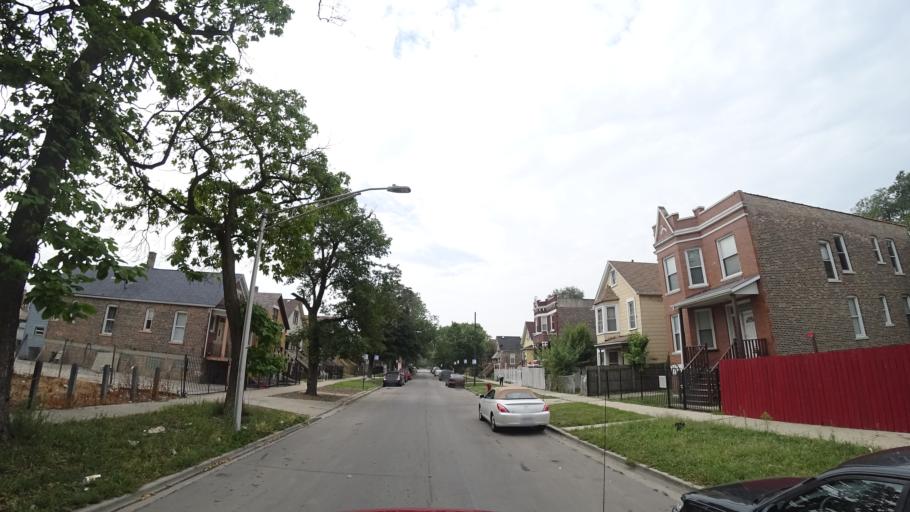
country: US
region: Illinois
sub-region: Cook County
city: Cicero
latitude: 41.8499
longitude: -87.7323
